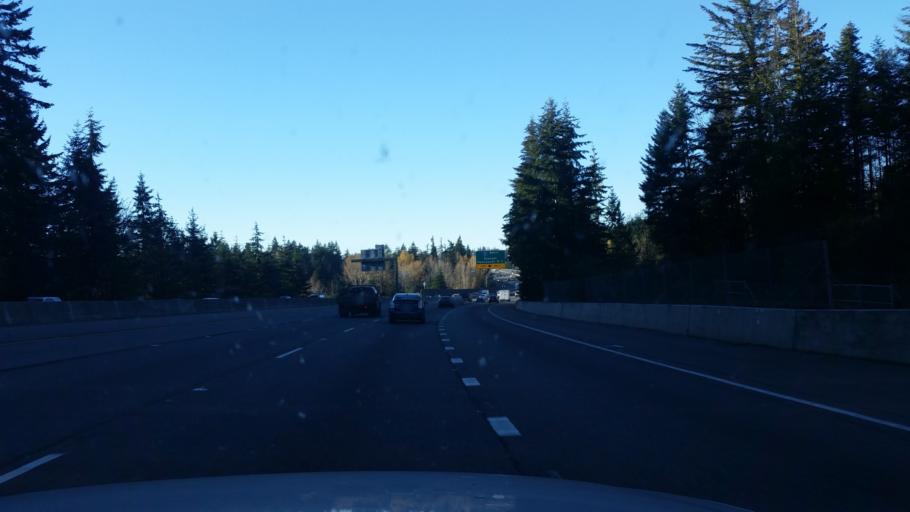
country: US
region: Washington
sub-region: Snohomish County
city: Martha Lake
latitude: 47.8242
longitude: -122.2520
